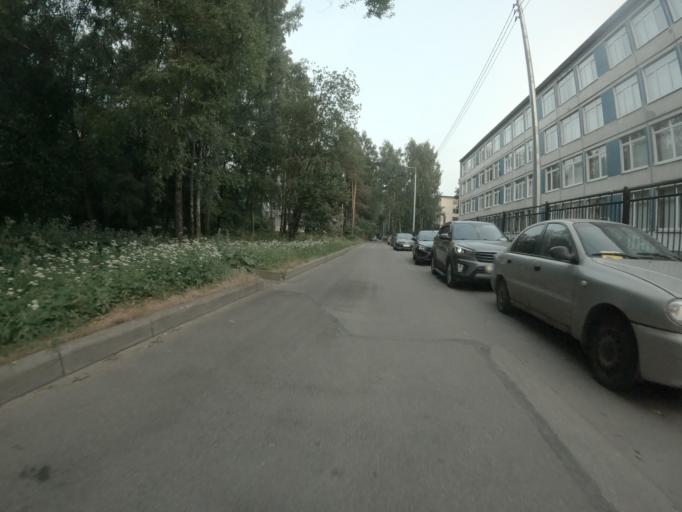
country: RU
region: St.-Petersburg
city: Krasnogvargeisky
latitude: 59.9570
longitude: 30.4442
